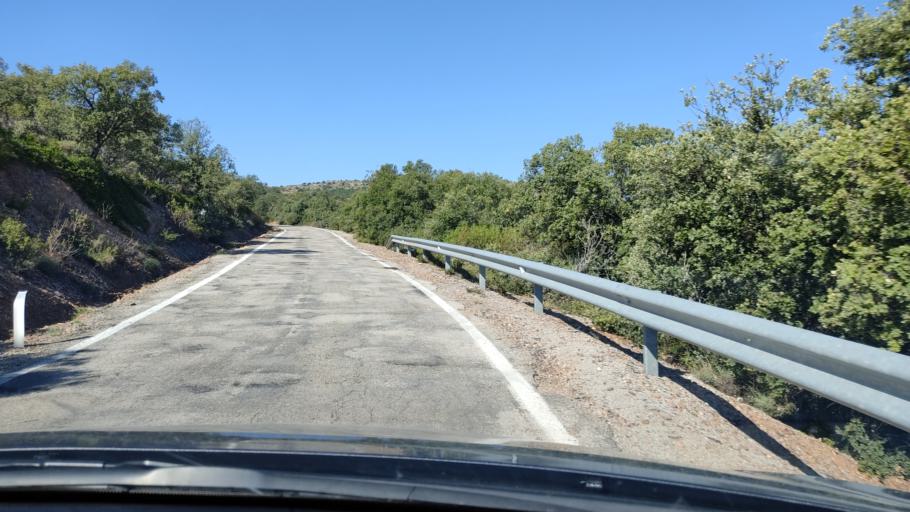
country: ES
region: Aragon
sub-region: Provincia de Teruel
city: Anadon
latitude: 41.0107
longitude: -0.9990
